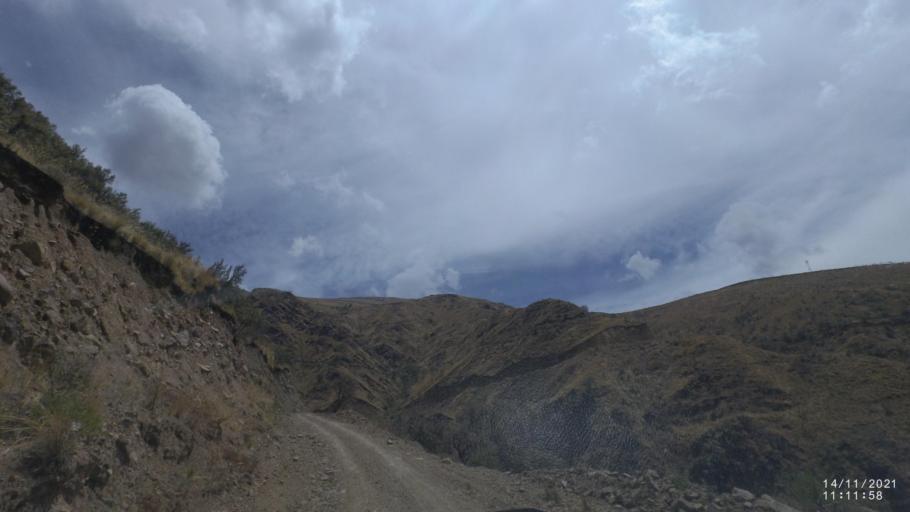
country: BO
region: Cochabamba
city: Cochabamba
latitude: -17.3282
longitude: -66.0507
